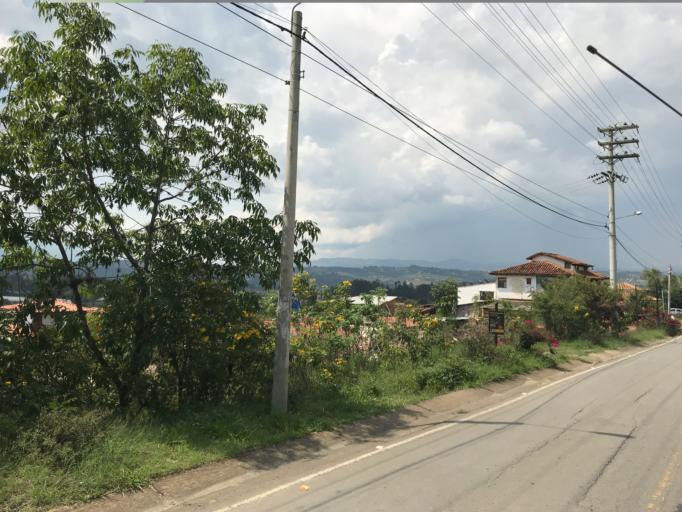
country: CO
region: Boyaca
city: Sachica
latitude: 5.6225
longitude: -73.5320
